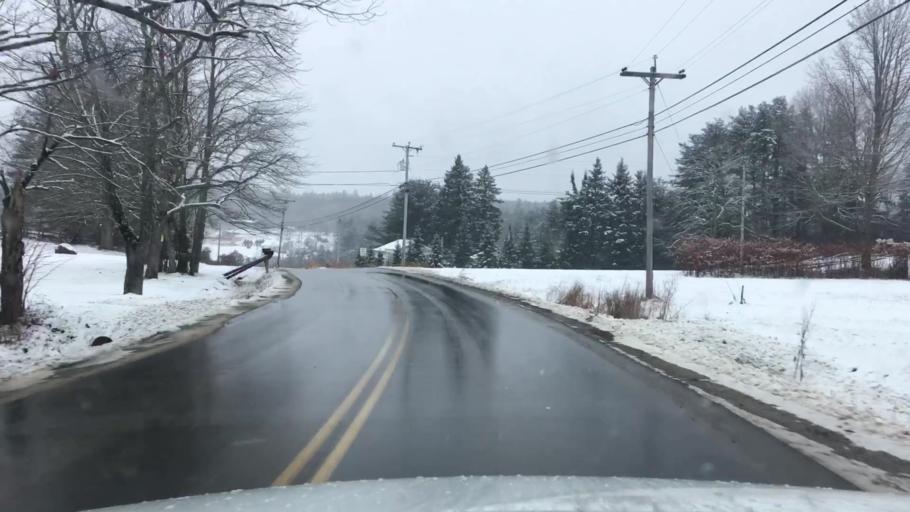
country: US
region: Maine
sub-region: Knox County
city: Warren
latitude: 44.1287
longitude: -69.2559
